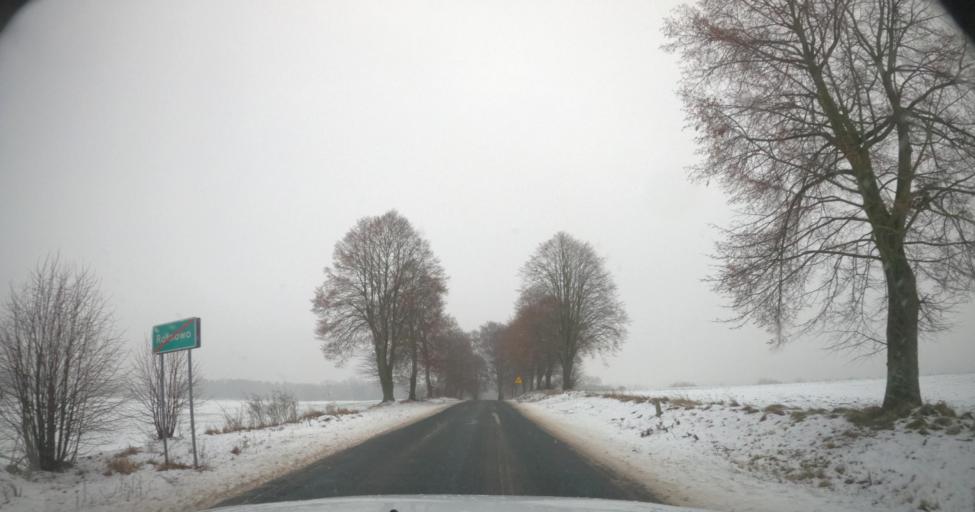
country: PL
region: West Pomeranian Voivodeship
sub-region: Powiat gryficki
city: Brojce
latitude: 53.9037
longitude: 15.2925
